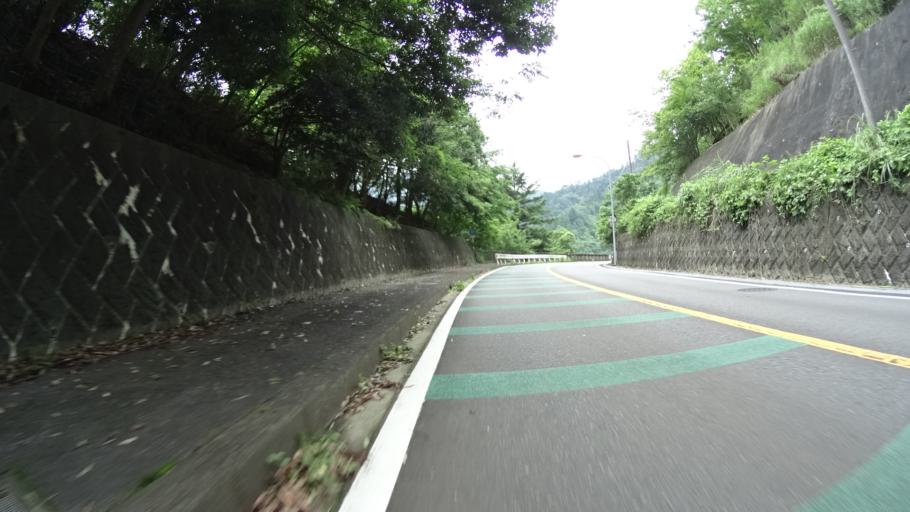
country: JP
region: Kanagawa
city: Hadano
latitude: 35.5071
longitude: 139.2309
